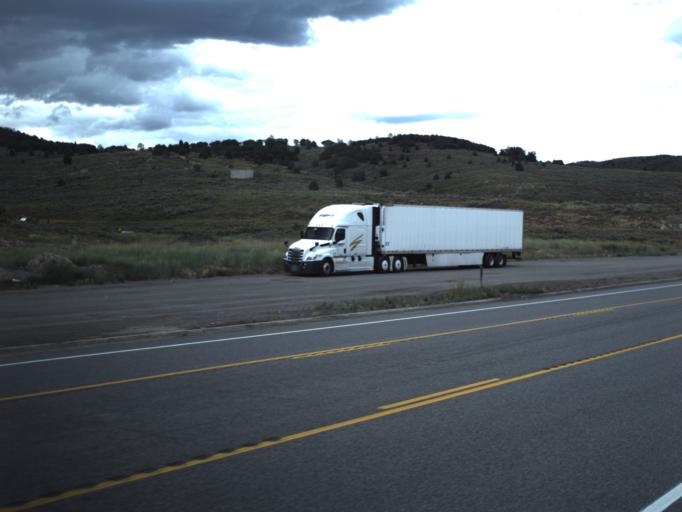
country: US
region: Utah
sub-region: Carbon County
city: Helper
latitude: 39.9285
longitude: -111.0781
